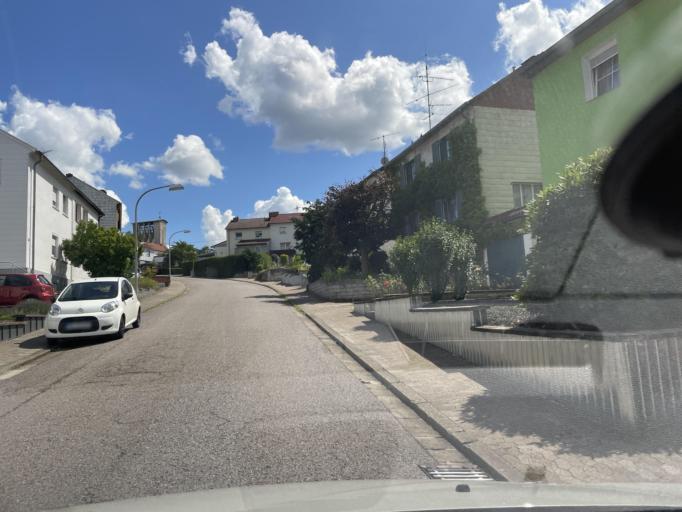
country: DE
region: Saarland
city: Sulzbach
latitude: 49.2742
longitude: 7.0505
